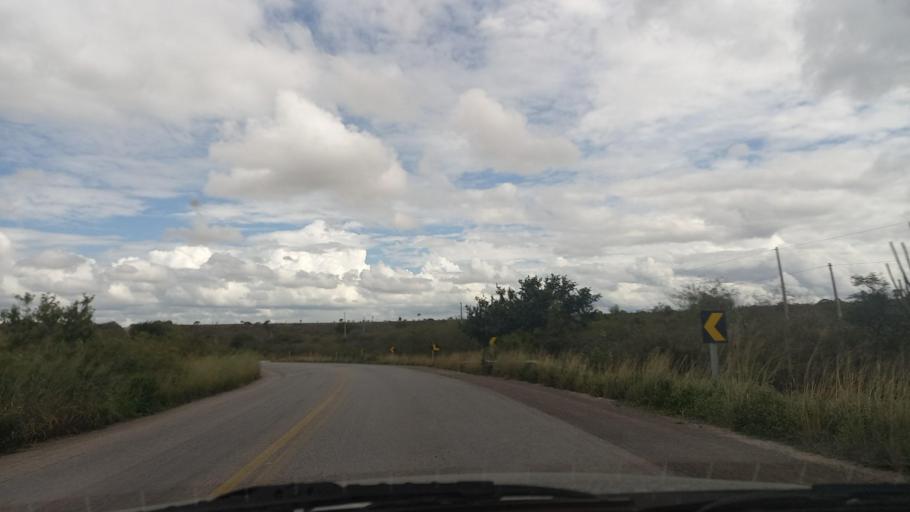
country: BR
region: Pernambuco
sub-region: Cachoeirinha
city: Cachoeirinha
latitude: -8.3531
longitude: -36.1715
